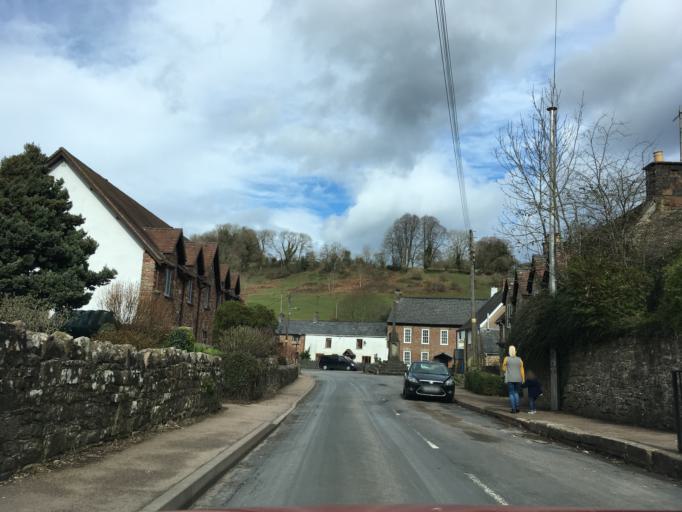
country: GB
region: England
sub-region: Gloucestershire
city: Coleford
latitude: 51.7691
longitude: -2.6222
